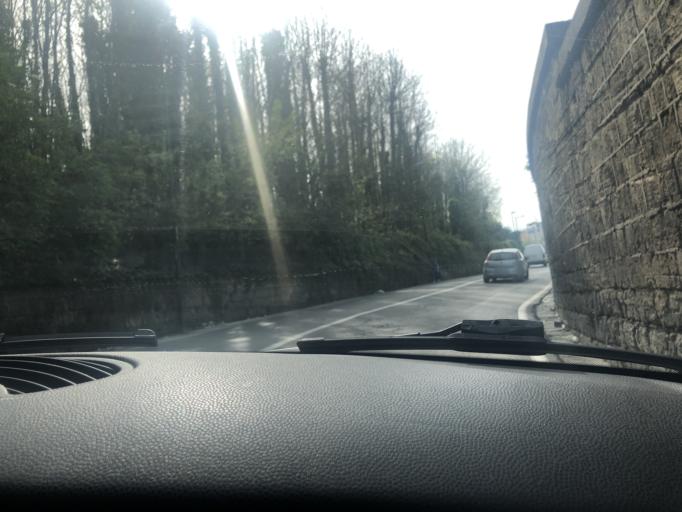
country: IT
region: Campania
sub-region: Provincia di Napoli
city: Torre Caracciolo
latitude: 40.8681
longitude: 14.2075
